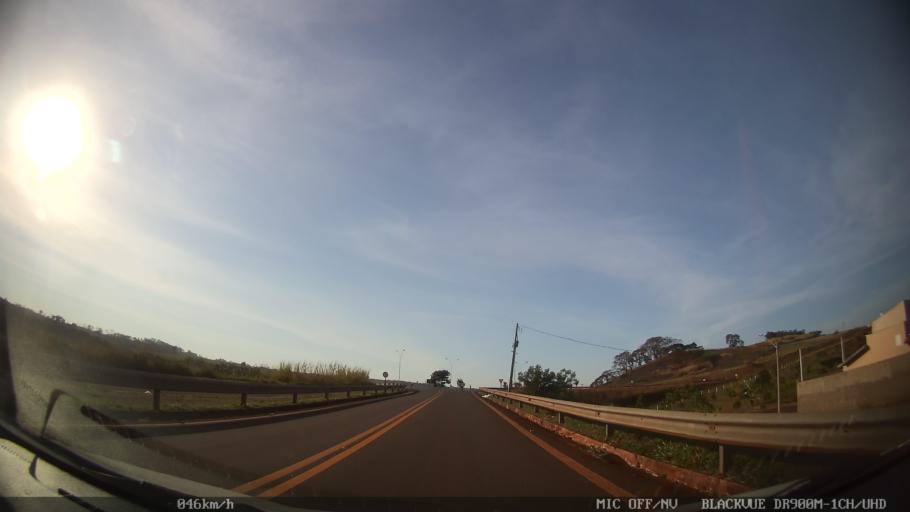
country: BR
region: Sao Paulo
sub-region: Cravinhos
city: Cravinhos
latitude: -21.2771
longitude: -47.8059
